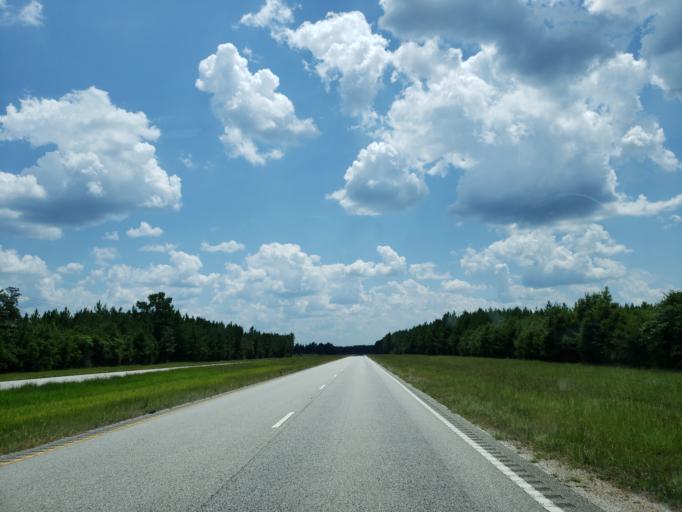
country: US
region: Mississippi
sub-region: Greene County
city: Leakesville
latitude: 31.2692
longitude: -88.5164
